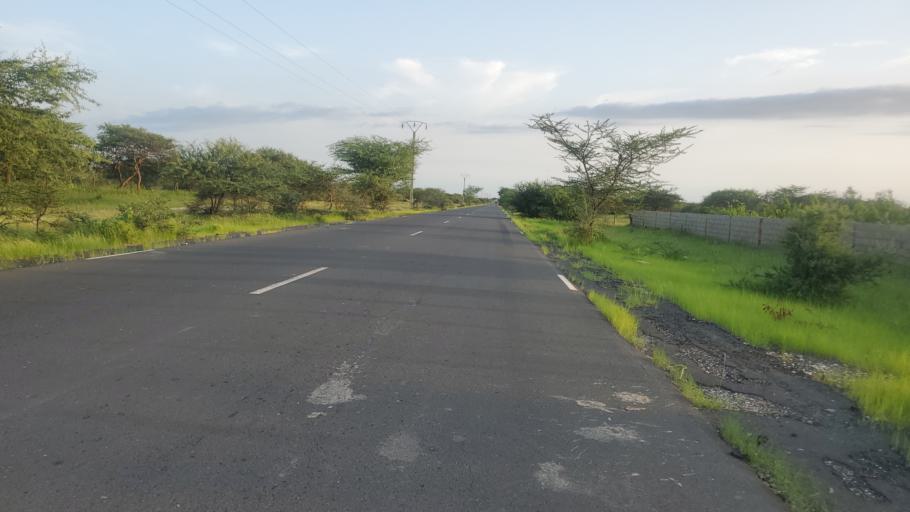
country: SN
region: Saint-Louis
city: Saint-Louis
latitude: 16.1739
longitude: -16.4097
